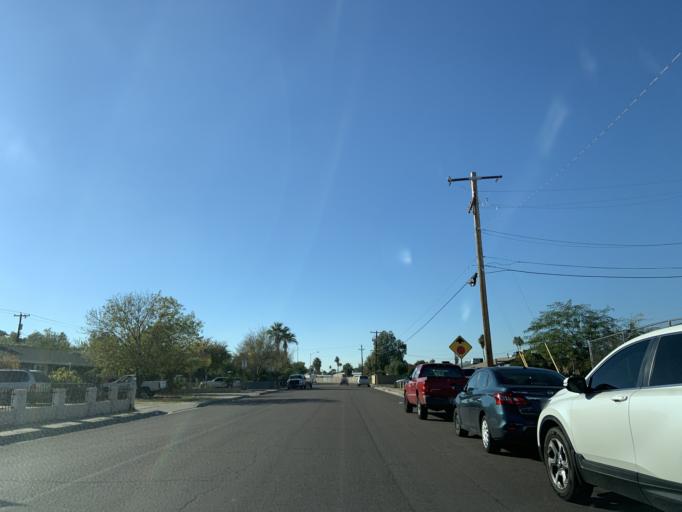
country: US
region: Arizona
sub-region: Maricopa County
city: Tempe
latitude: 33.4008
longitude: -111.8683
